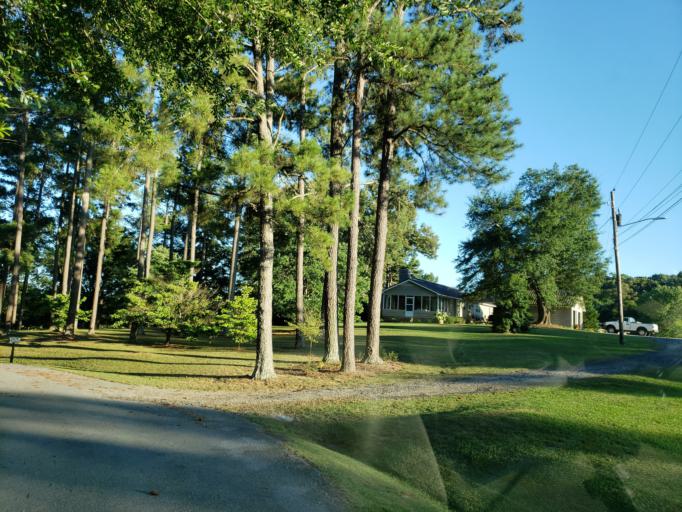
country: US
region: Georgia
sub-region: Polk County
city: Aragon
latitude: 34.0919
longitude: -84.9937
